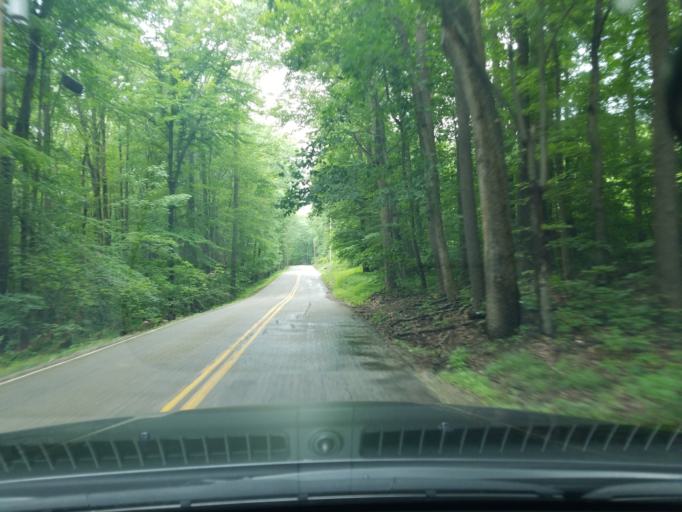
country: US
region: Pennsylvania
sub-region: Fayette County
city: Bear Rocks
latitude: 40.1842
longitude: -79.3789
